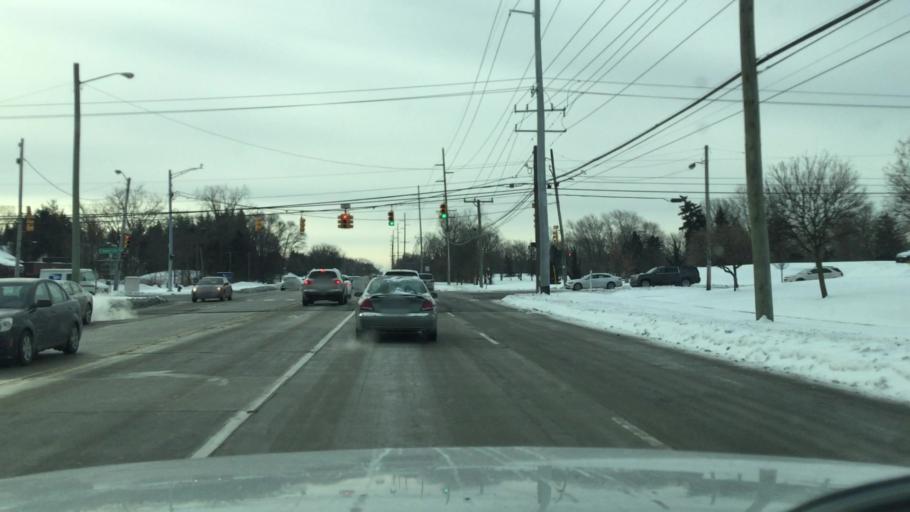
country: US
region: Michigan
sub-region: Oakland County
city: Troy
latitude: 42.6076
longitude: -83.1299
